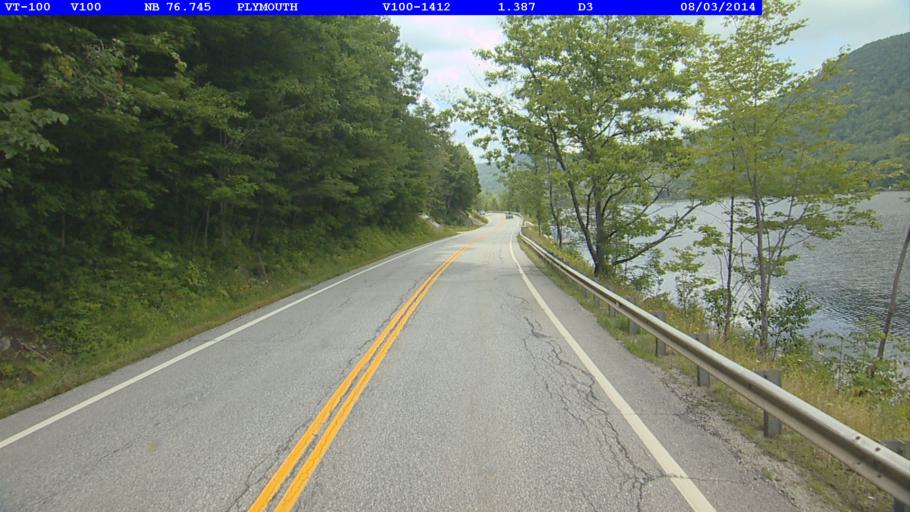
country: US
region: Vermont
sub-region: Windsor County
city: Woodstock
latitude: 43.4825
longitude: -72.7047
